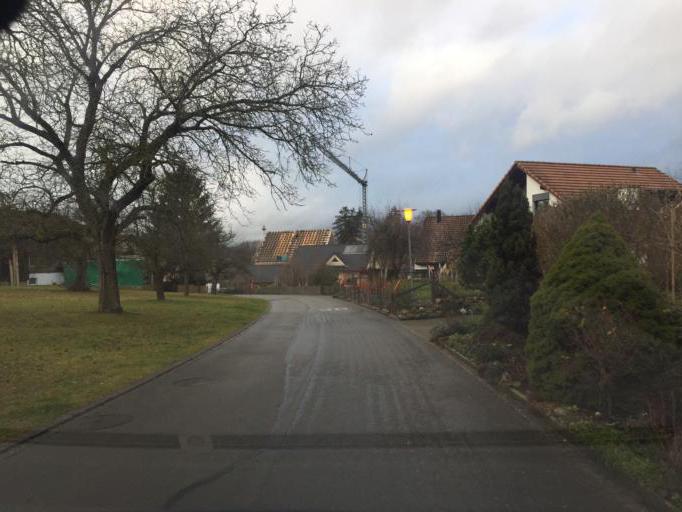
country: CH
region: Thurgau
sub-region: Frauenfeld District
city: Diessenhofen
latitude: 47.6658
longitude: 8.7482
